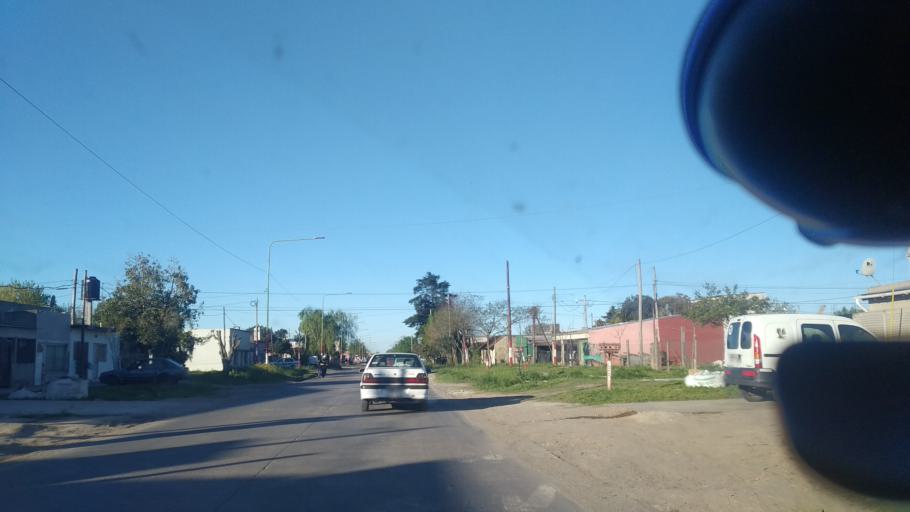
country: AR
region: Buenos Aires
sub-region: Partido de La Plata
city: La Plata
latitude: -34.9647
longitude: -57.9648
